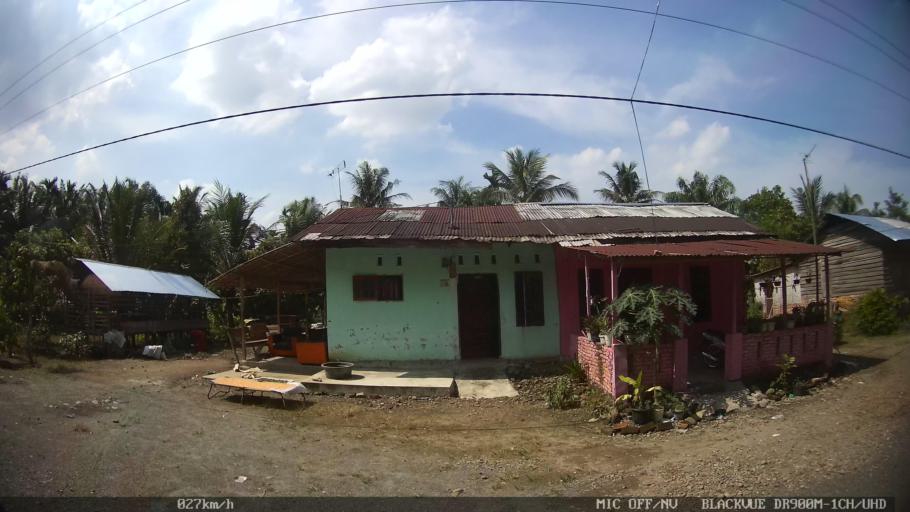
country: ID
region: North Sumatra
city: Binjai
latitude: 3.6344
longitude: 98.5268
